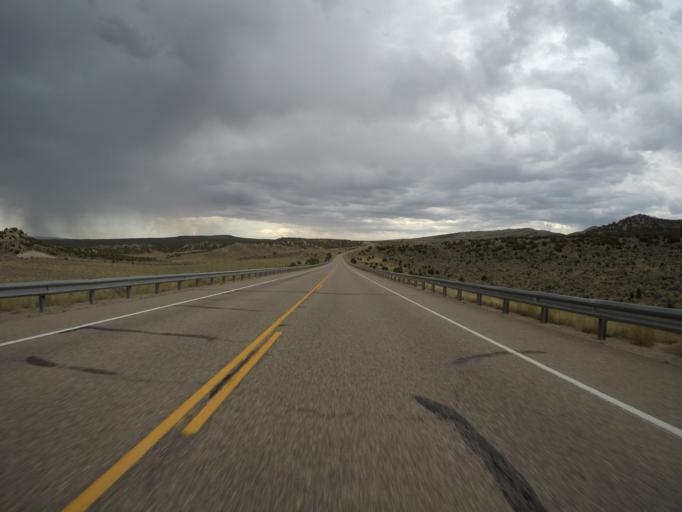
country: US
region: Colorado
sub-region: Rio Blanco County
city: Rangely
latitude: 40.3649
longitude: -108.4166
